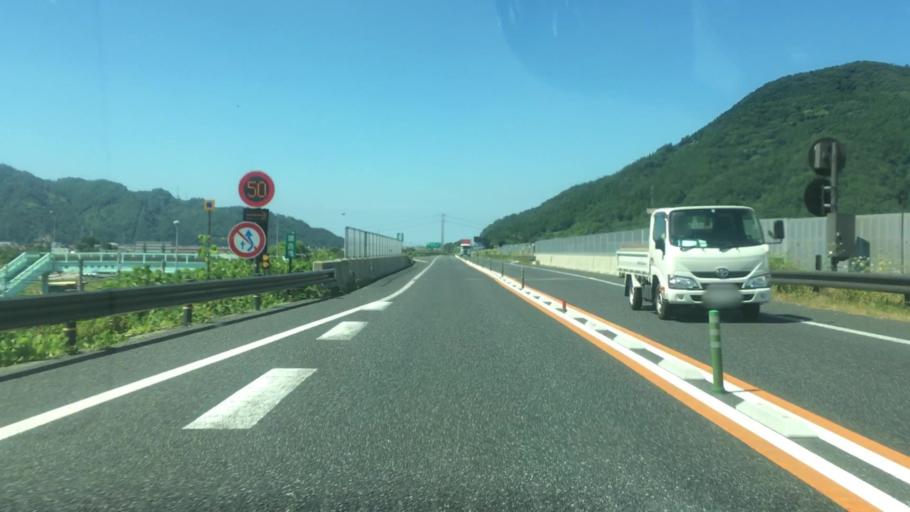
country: JP
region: Tottori
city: Tottori
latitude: 35.3993
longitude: 134.2049
